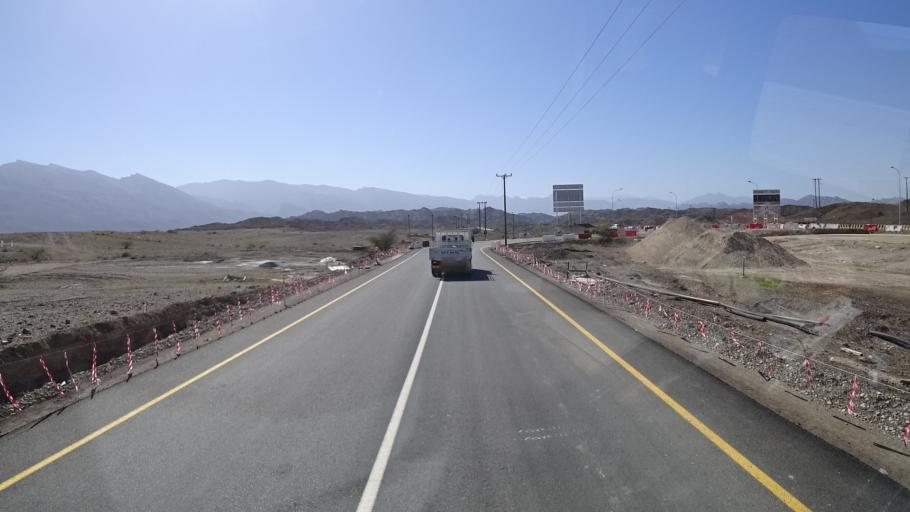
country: OM
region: Al Batinah
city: Bayt al `Awabi
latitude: 23.3733
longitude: 57.6900
